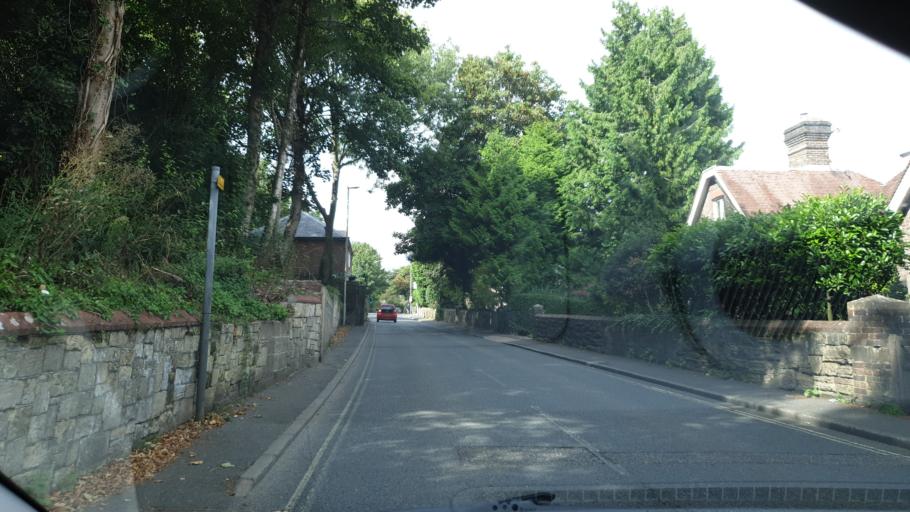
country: GB
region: England
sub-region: West Sussex
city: East Grinstead
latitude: 51.1247
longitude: -0.0033
